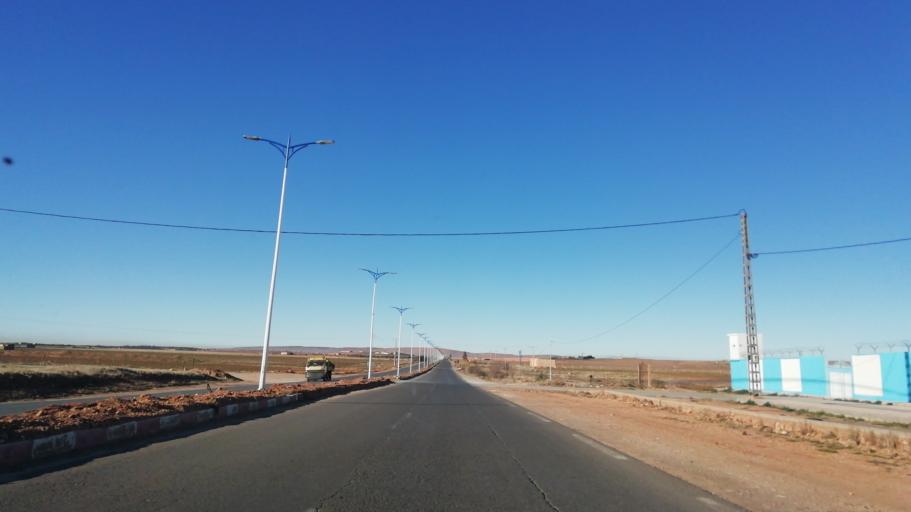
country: DZ
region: El Bayadh
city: El Bayadh
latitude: 33.6908
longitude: 1.0724
